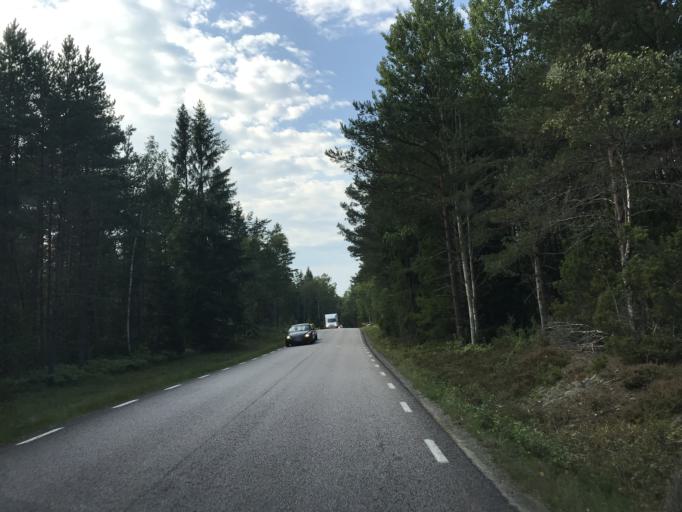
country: SE
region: Stockholm
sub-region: Norrtalje Kommun
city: Bjorko
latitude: 59.8863
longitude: 18.9791
